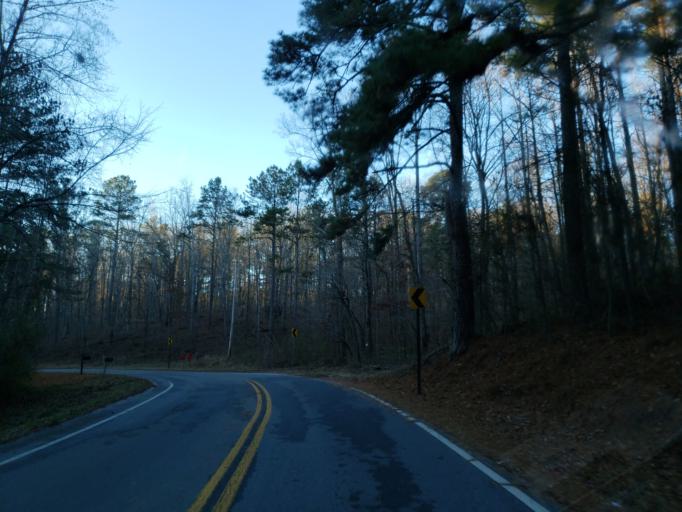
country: US
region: Georgia
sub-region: Paulding County
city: Hiram
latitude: 33.9070
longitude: -84.7636
